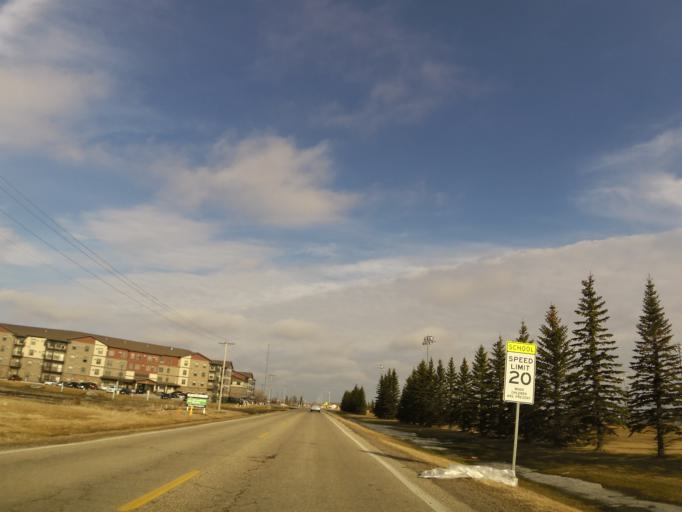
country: US
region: North Dakota
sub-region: Grand Forks County
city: Grand Forks
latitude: 47.8750
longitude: -97.0625
